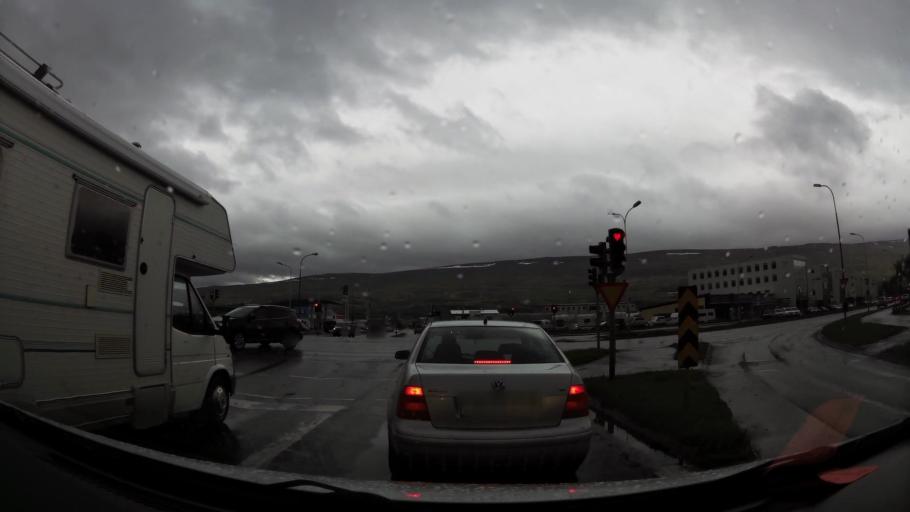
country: IS
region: Northeast
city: Akureyri
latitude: 65.6884
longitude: -18.1018
